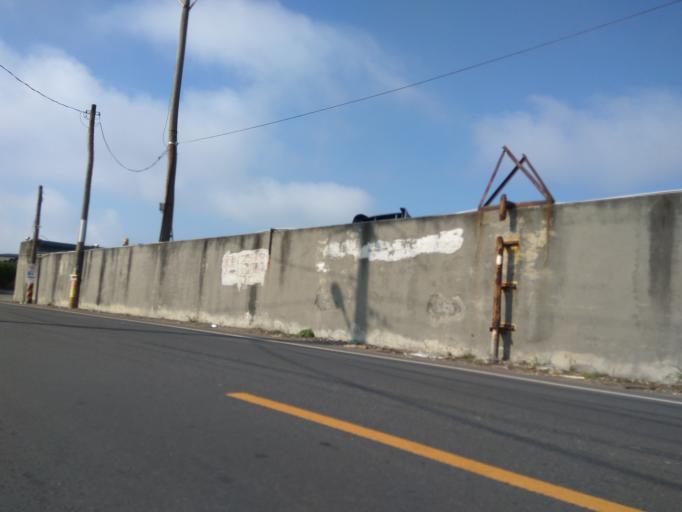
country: TW
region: Taiwan
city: Taoyuan City
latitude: 25.0780
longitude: 121.1749
